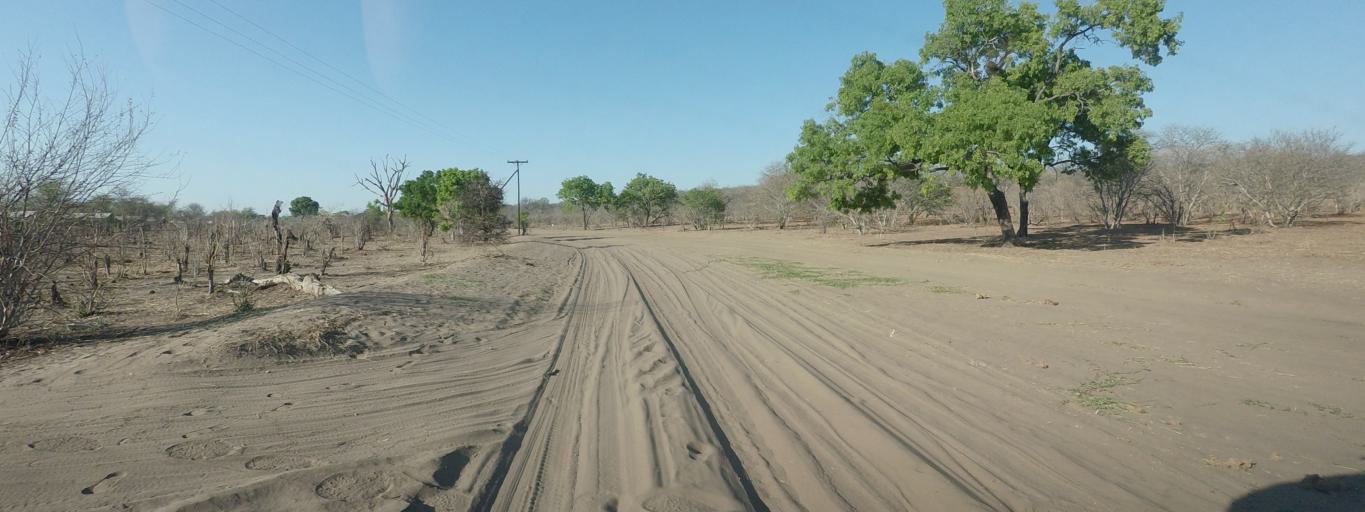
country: BW
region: North West
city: Kasane
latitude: -17.8865
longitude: 25.2301
